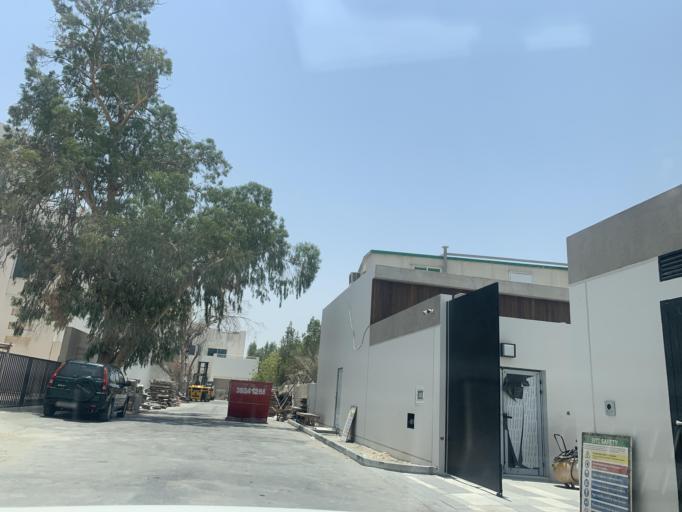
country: BH
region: Manama
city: Jidd Hafs
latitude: 26.2070
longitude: 50.4774
